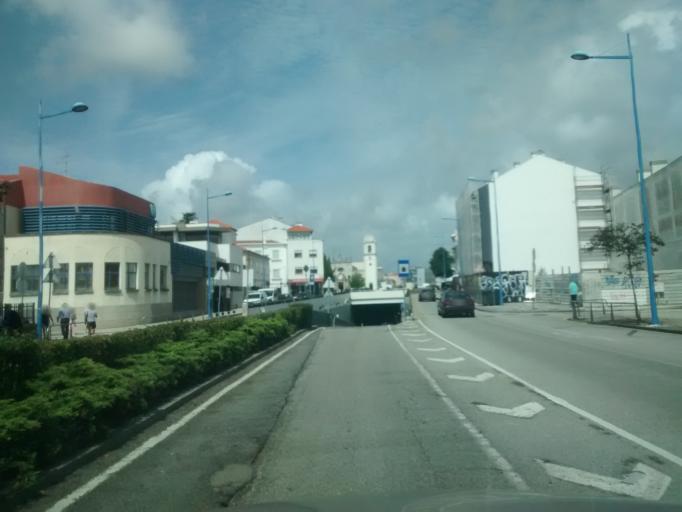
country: PT
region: Aveiro
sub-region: Aveiro
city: Aveiro
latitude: 40.6377
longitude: -8.6524
